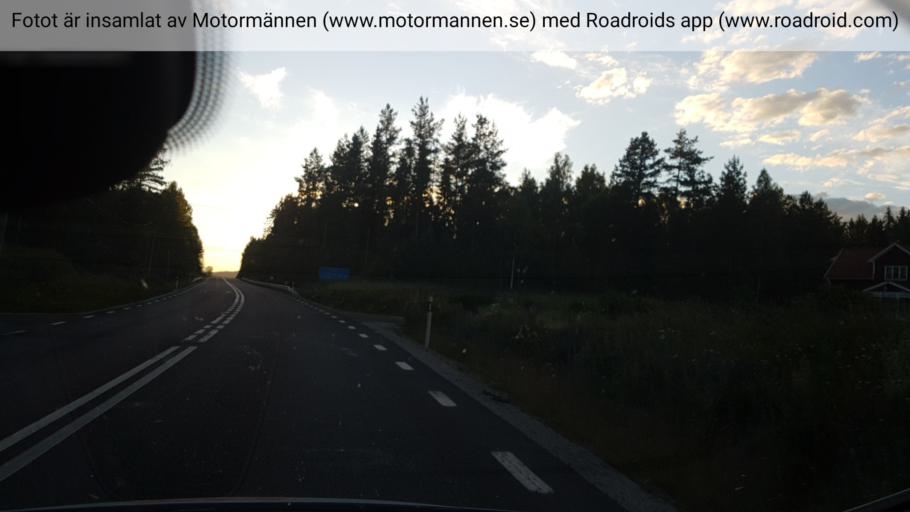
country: SE
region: Vaermland
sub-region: Sunne Kommun
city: Sunne
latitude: 59.6568
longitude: 12.9403
